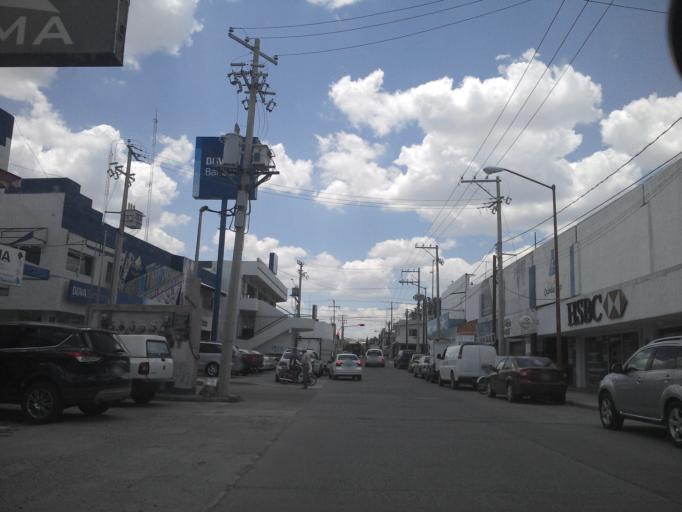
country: MX
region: Guanajuato
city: San Francisco del Rincon
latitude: 21.0280
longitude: -101.8579
